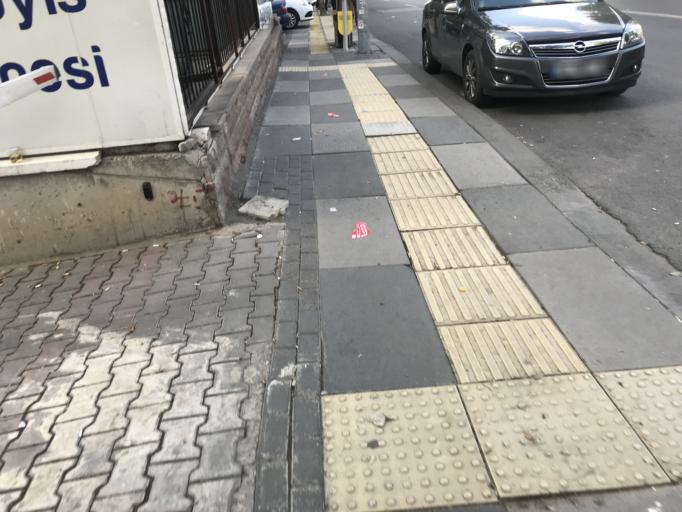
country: TR
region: Ankara
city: Ankara
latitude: 39.8754
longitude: 32.8347
